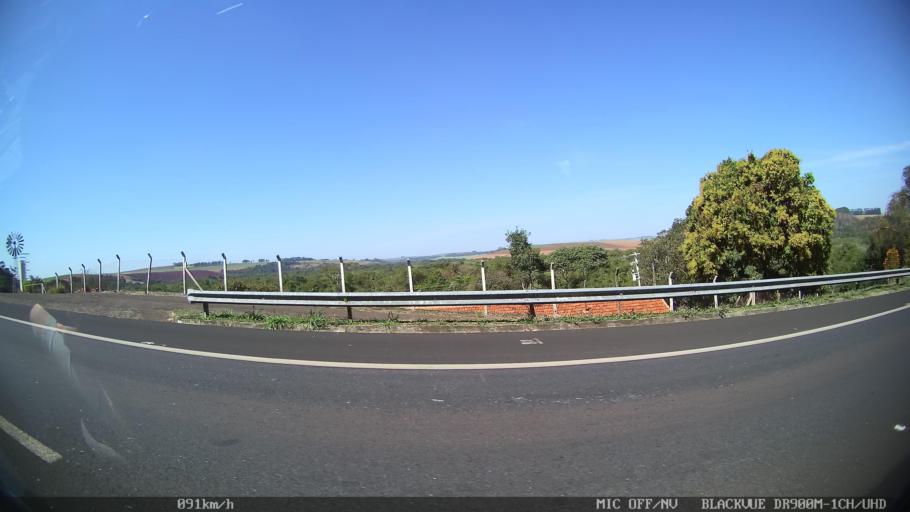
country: BR
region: Sao Paulo
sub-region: Batatais
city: Batatais
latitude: -20.7252
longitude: -47.5158
